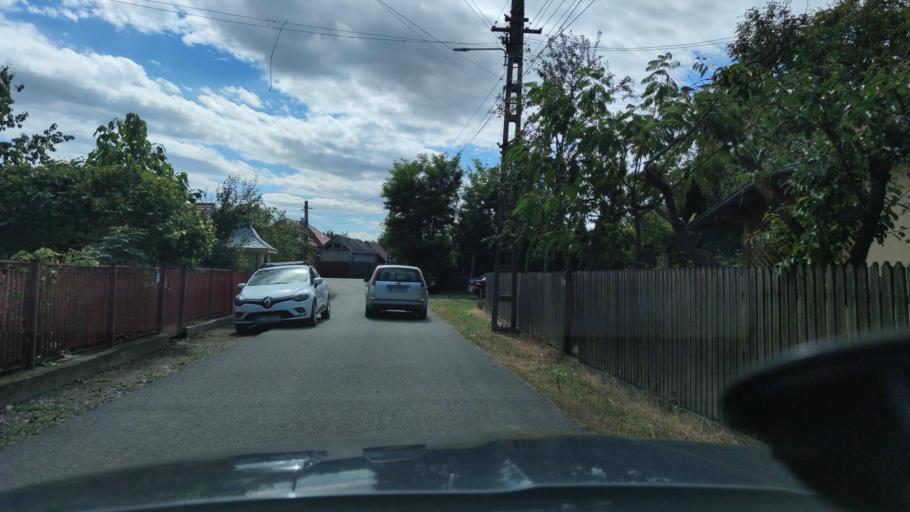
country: RO
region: Buzau
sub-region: Comuna Beceni
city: Valea Parului
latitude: 45.3714
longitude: 26.7697
